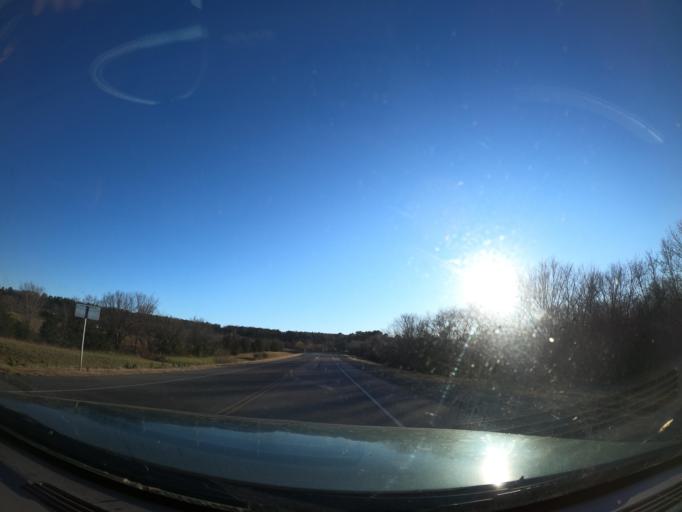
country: US
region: Oklahoma
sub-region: Pittsburg County
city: Hartshorne
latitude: 34.8431
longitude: -95.5392
